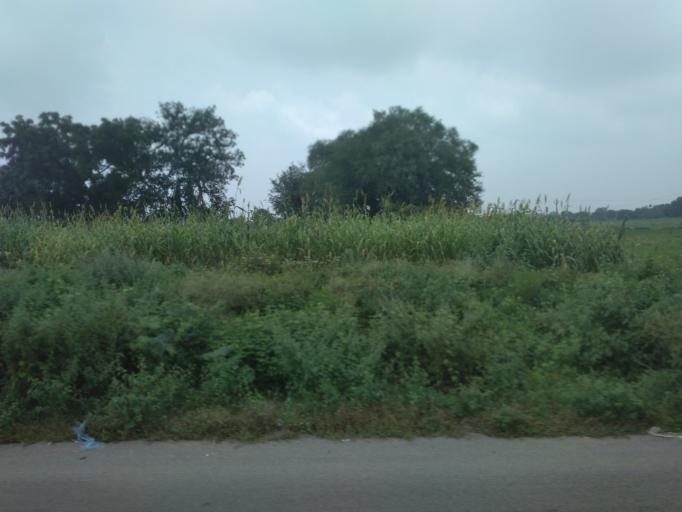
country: IN
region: Telangana
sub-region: Warangal
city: Jangaon
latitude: 17.6806
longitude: 79.1107
